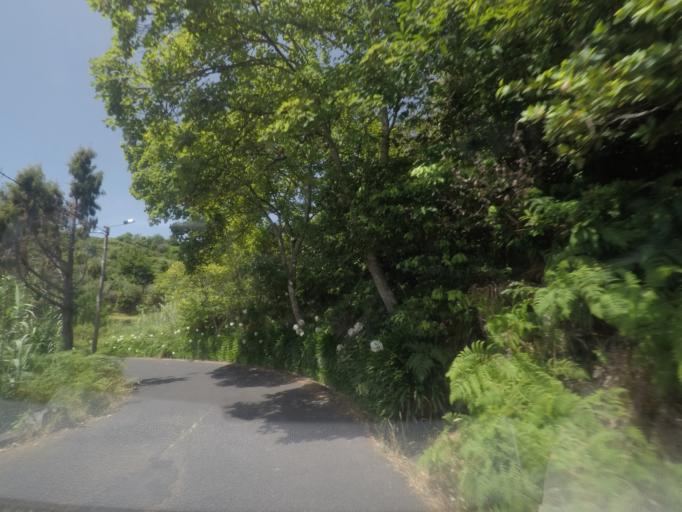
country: PT
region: Madeira
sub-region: Calheta
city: Faja da Ovelha
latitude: 32.7655
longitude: -17.2062
